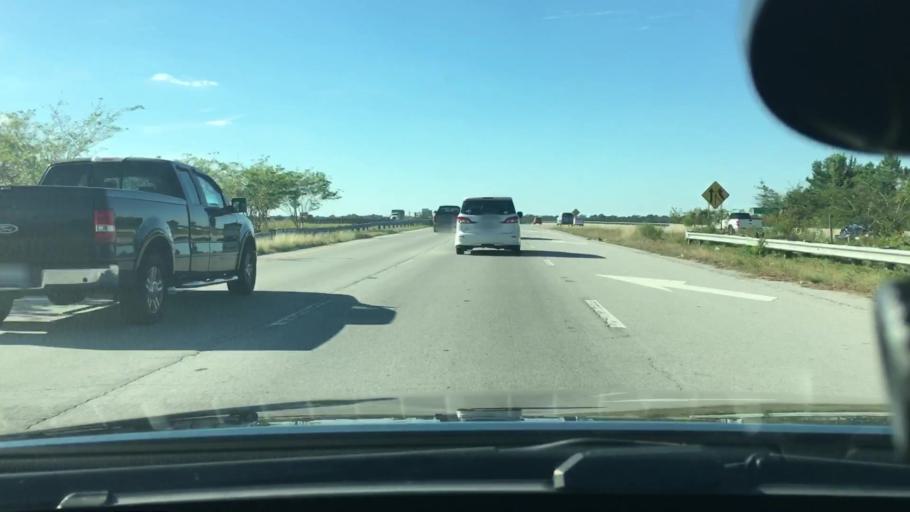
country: US
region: North Carolina
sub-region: Craven County
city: James City
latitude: 35.0949
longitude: -77.0419
